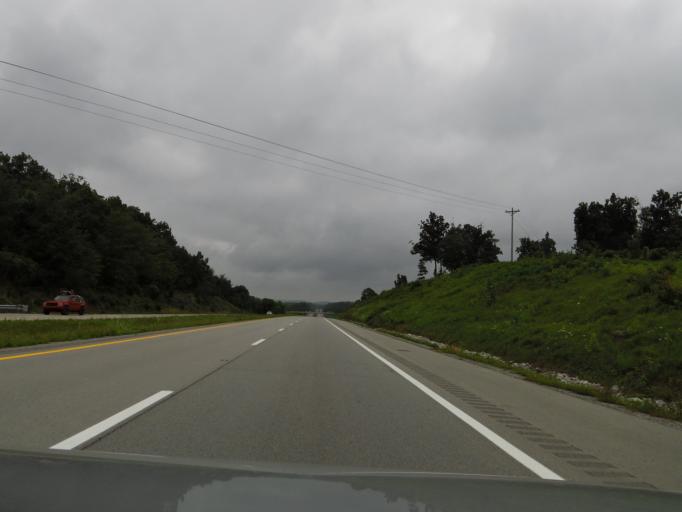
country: US
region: Kentucky
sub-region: Grayson County
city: Leitchfield
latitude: 37.4124
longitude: -86.4939
